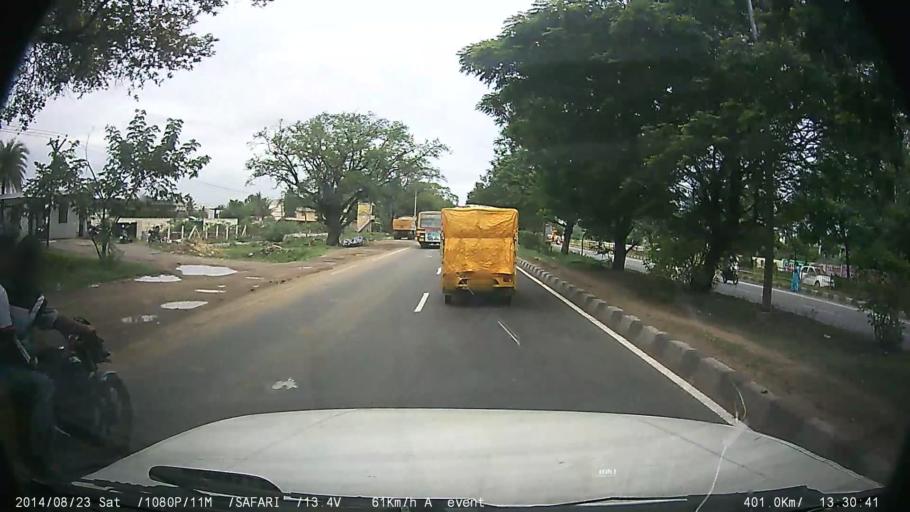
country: IN
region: Tamil Nadu
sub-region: Kancheepuram
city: Vandalur
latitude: 12.8744
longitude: 80.0782
